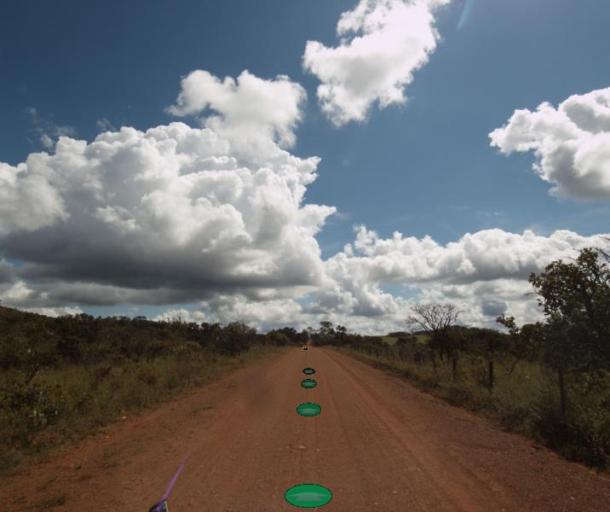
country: BR
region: Goias
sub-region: Pirenopolis
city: Pirenopolis
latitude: -15.7804
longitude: -48.8426
